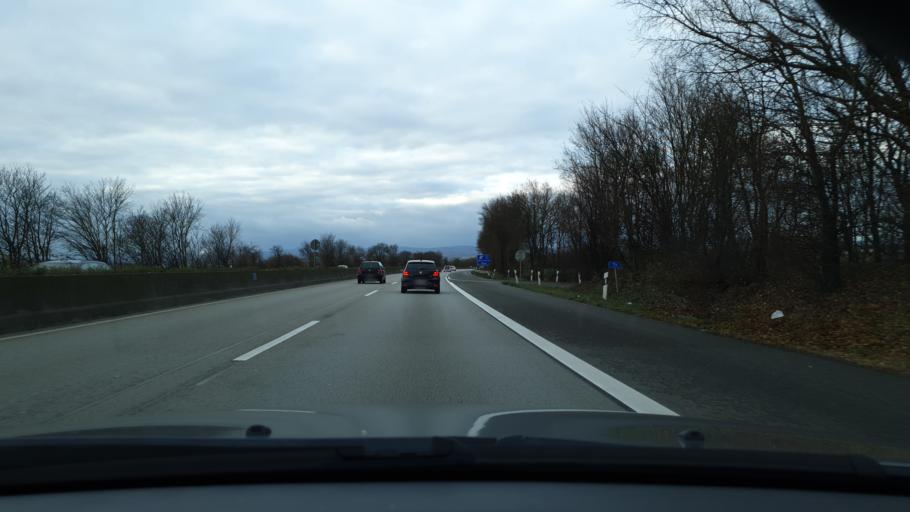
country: DE
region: Hesse
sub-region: Regierungsbezirk Darmstadt
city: Hochheim am Main
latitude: 50.0265
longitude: 8.3099
